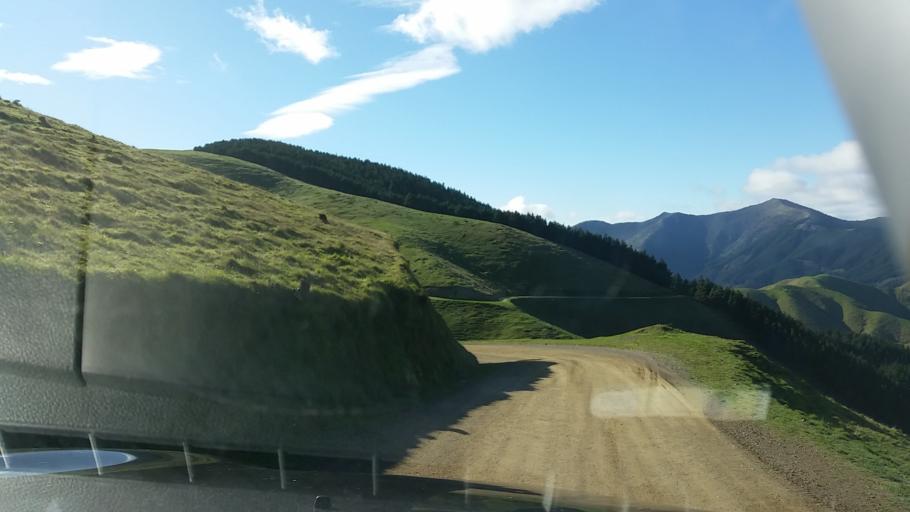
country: NZ
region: Marlborough
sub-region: Marlborough District
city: Picton
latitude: -40.9880
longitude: 173.8078
